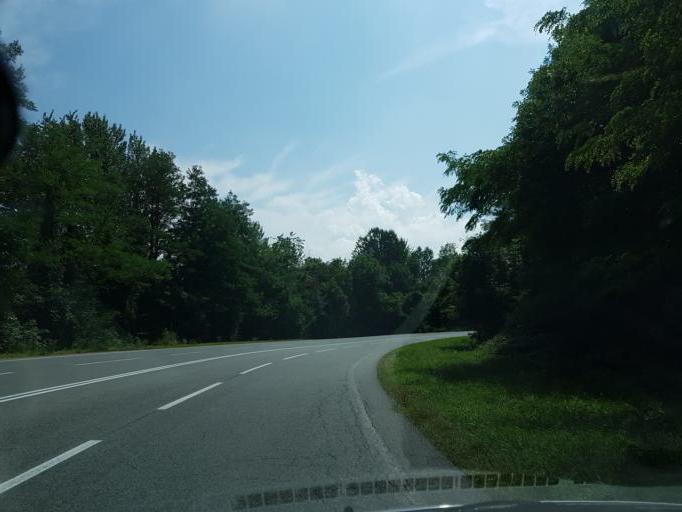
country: IT
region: Piedmont
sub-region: Provincia di Cuneo
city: Borgo San Dalmazzo
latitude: 44.3449
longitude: 7.4770
